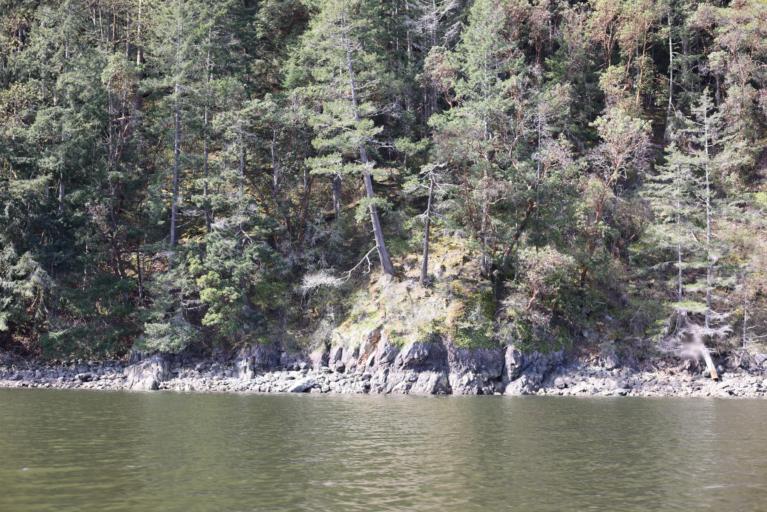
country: CA
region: British Columbia
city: Langford
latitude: 48.5362
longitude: -123.5544
